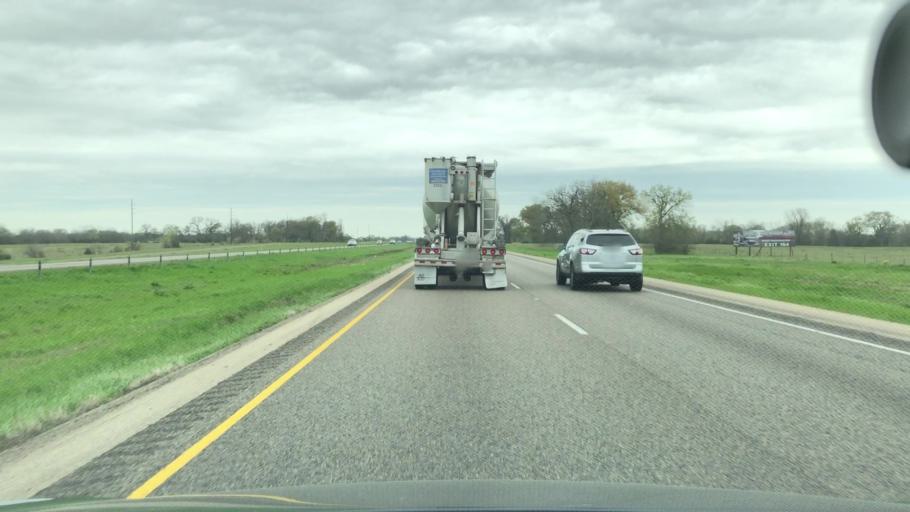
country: US
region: Texas
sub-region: Madison County
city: Madisonville
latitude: 31.0532
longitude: -95.9472
